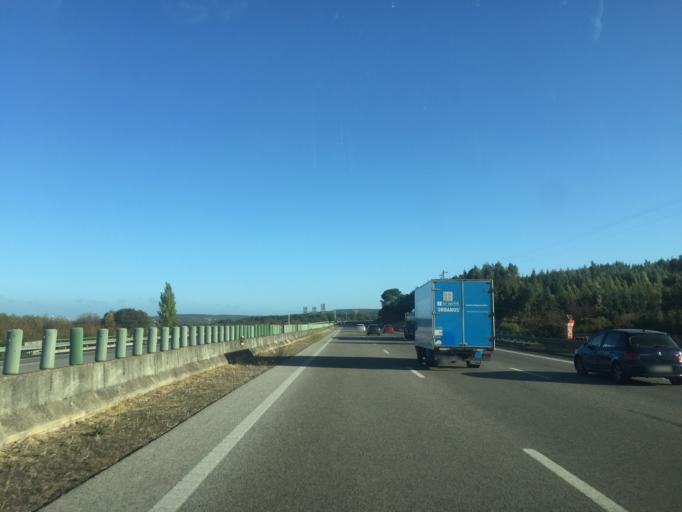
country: PT
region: Lisbon
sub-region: Alenquer
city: Carregado
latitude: 39.0618
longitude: -8.9407
